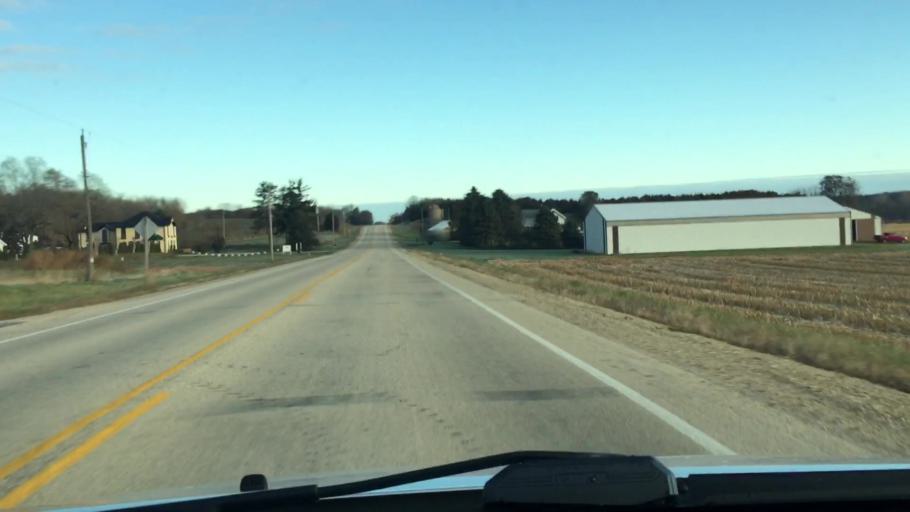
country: US
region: Wisconsin
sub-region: Washington County
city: Hartford
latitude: 43.2704
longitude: -88.4636
